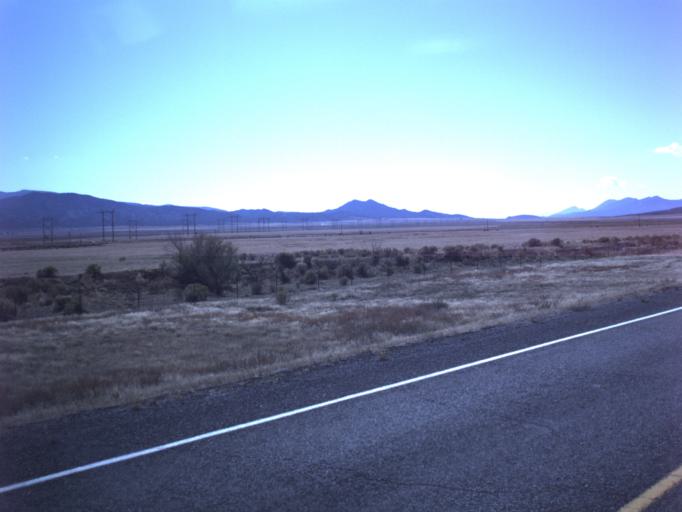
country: US
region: Utah
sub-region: Juab County
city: Nephi
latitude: 39.5270
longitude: -111.9346
